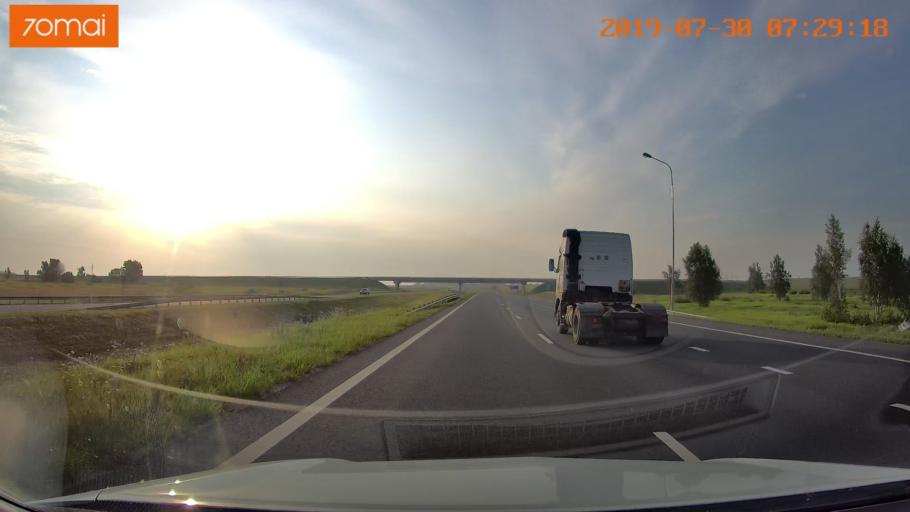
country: RU
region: Kaliningrad
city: Gvardeysk
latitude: 54.6730
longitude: 20.9358
